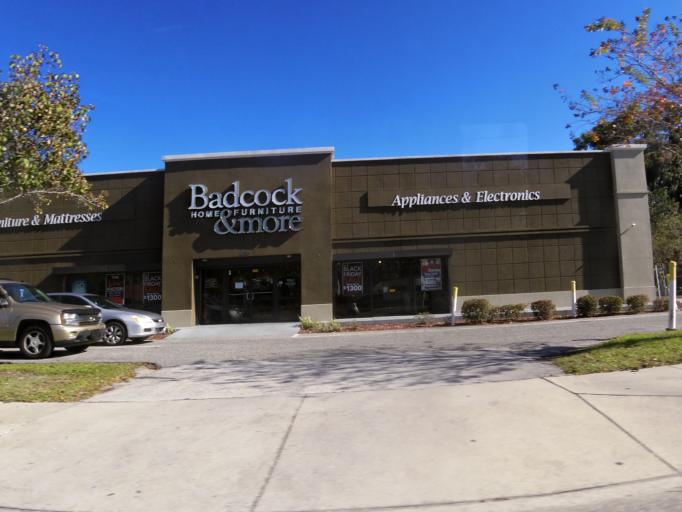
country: US
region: Florida
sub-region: Duval County
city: Jacksonville
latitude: 30.3795
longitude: -81.6503
